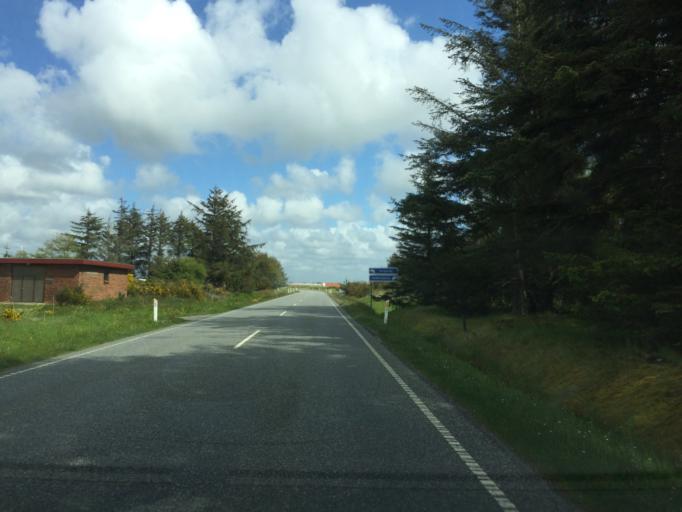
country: DK
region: Central Jutland
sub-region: Holstebro Kommune
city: Ulfborg
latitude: 56.3199
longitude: 8.1362
